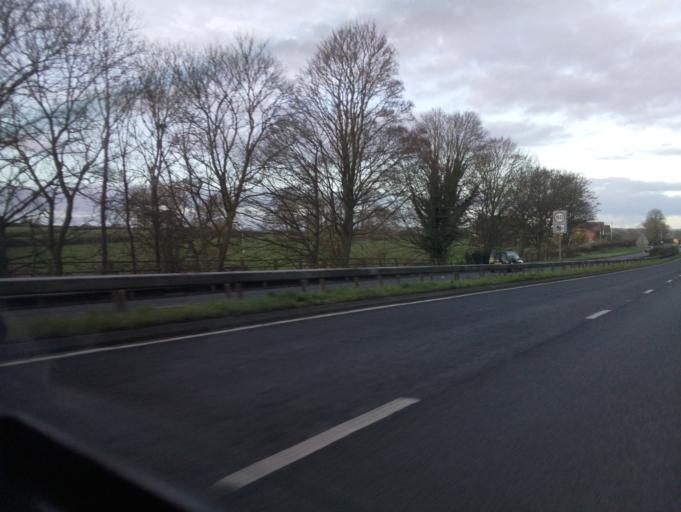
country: GB
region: England
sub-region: Staffordshire
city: Stone
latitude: 52.8635
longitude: -2.1316
